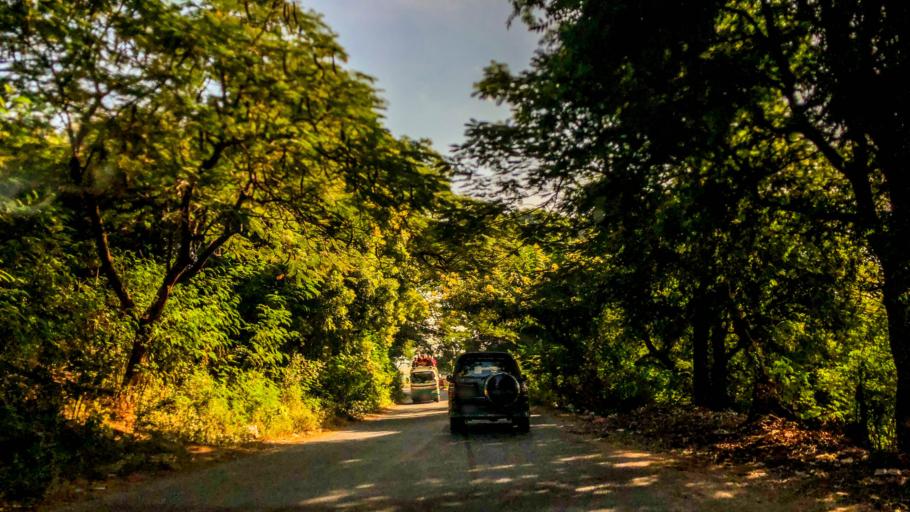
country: MM
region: Sagain
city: Sagaing
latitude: 21.8669
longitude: 95.9985
